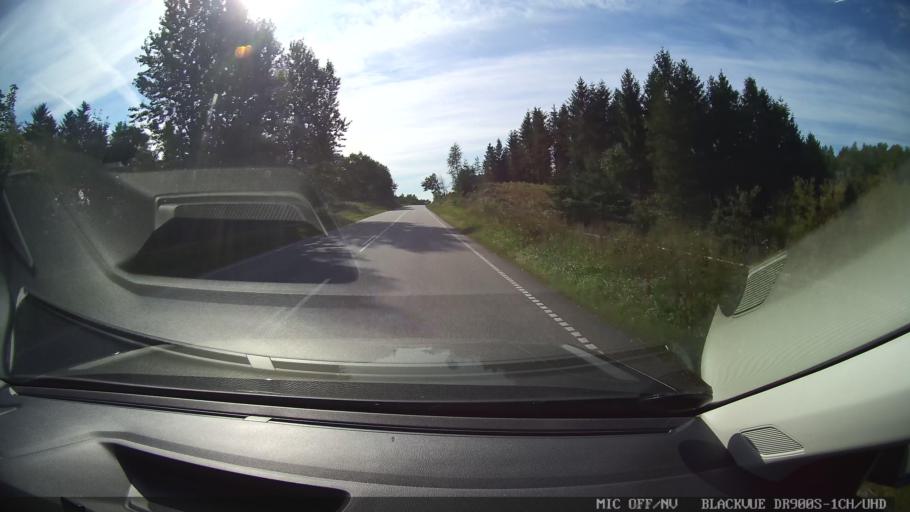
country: DK
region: North Denmark
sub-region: Mariagerfjord Kommune
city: Hadsund
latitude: 56.7558
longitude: 10.0705
